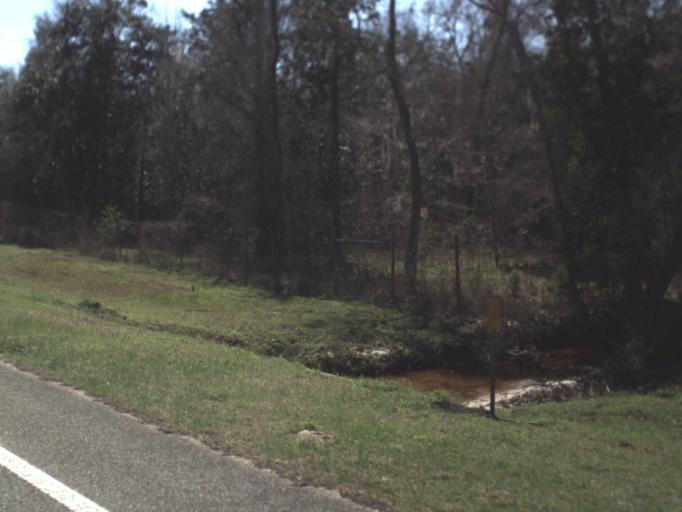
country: US
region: Florida
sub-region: Calhoun County
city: Blountstown
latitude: 30.5859
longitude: -85.0228
